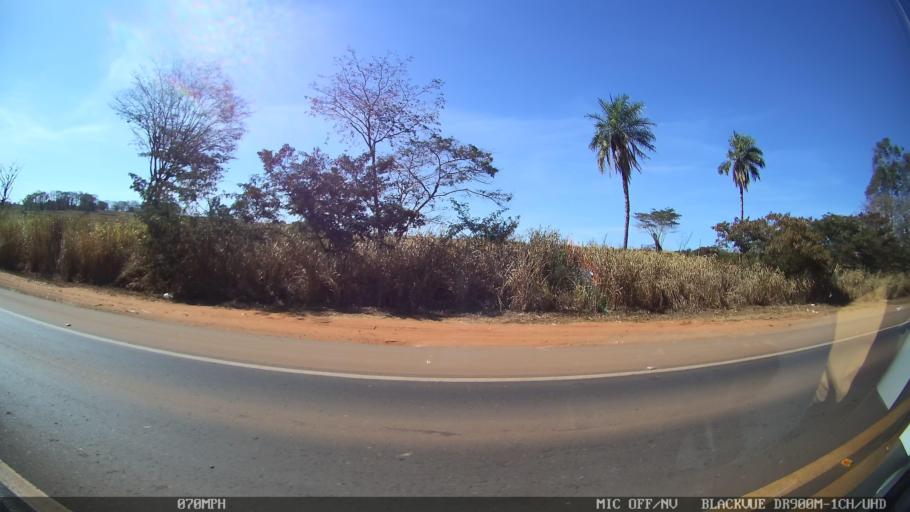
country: BR
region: Sao Paulo
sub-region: Olimpia
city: Olimpia
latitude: -20.6991
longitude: -48.8907
